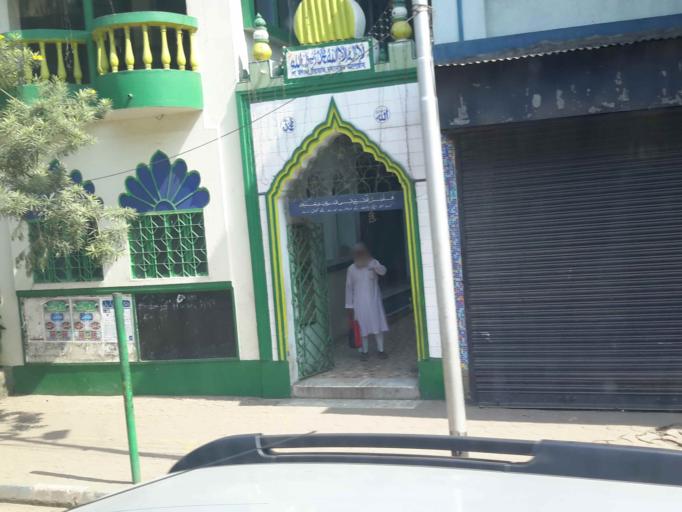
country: IN
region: West Bengal
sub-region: Kolkata
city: Kolkata
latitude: 22.5413
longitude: 88.3653
